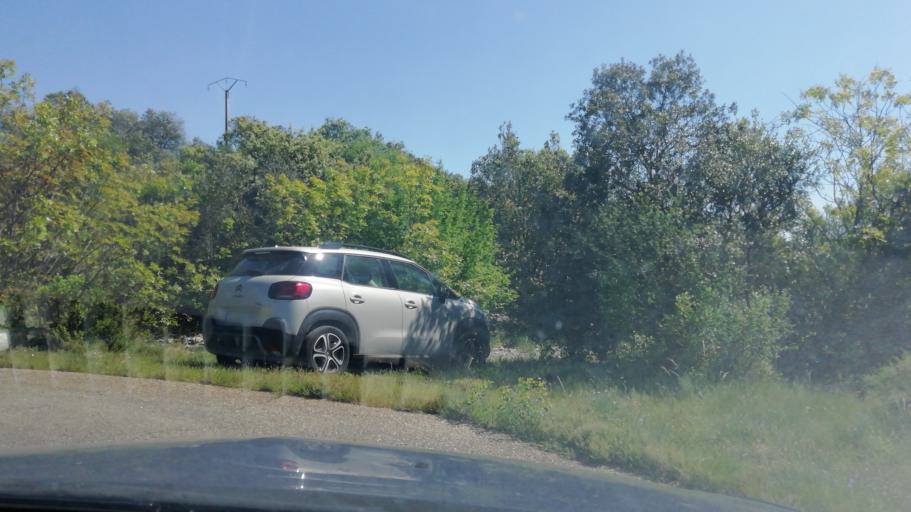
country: FR
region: Languedoc-Roussillon
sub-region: Departement de l'Herault
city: Saint-Mathieu-de-Treviers
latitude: 43.8357
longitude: 3.8208
